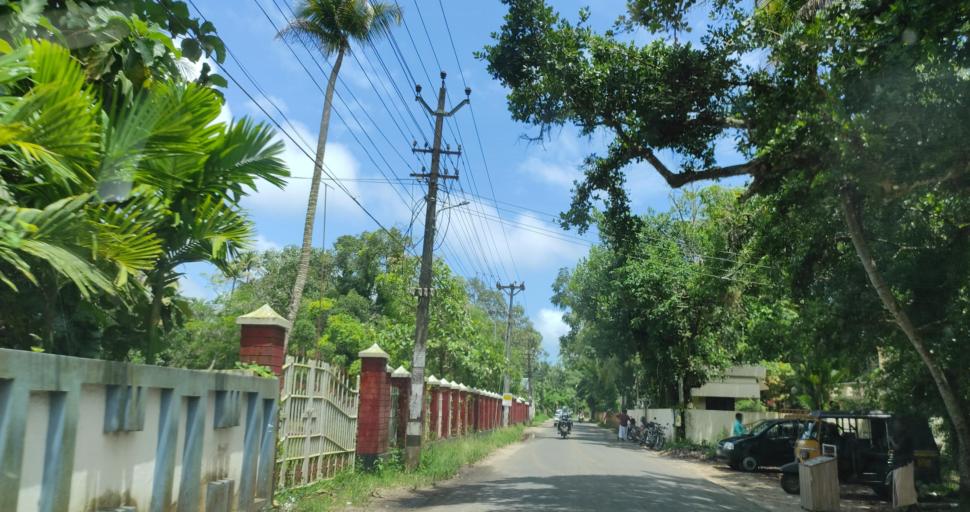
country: IN
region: Kerala
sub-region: Alappuzha
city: Vayalar
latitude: 9.7038
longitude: 76.3388
